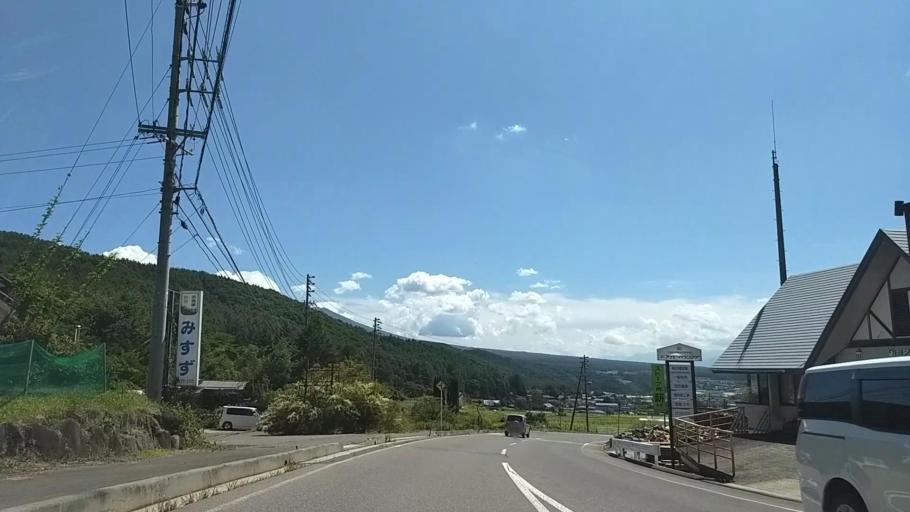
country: JP
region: Nagano
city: Chino
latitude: 36.0627
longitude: 138.2231
